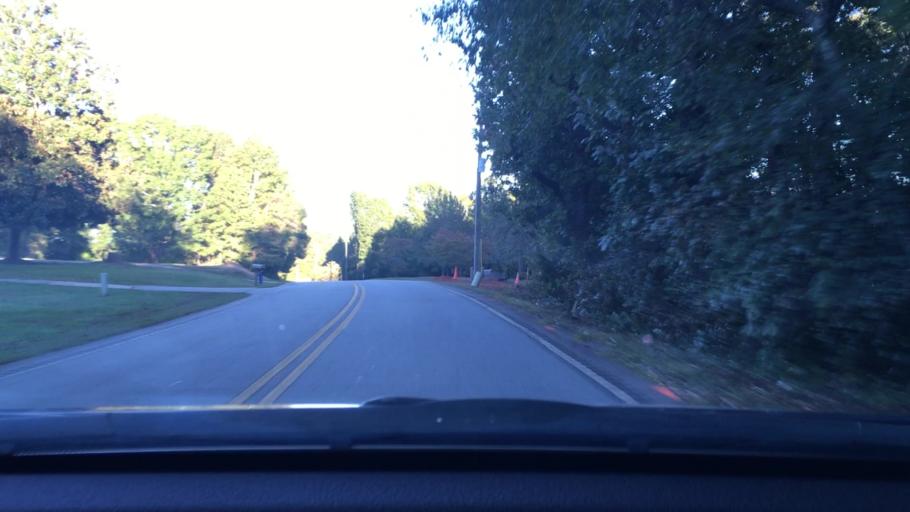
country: US
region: South Carolina
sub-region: Lexington County
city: Irmo
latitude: 34.1253
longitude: -81.1917
